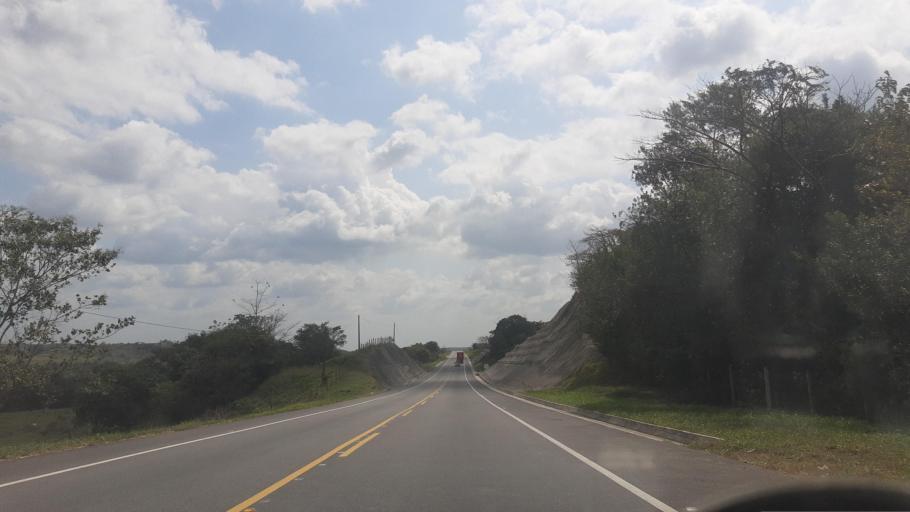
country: CO
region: Casanare
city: Monterrey
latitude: 4.8233
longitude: -72.8070
